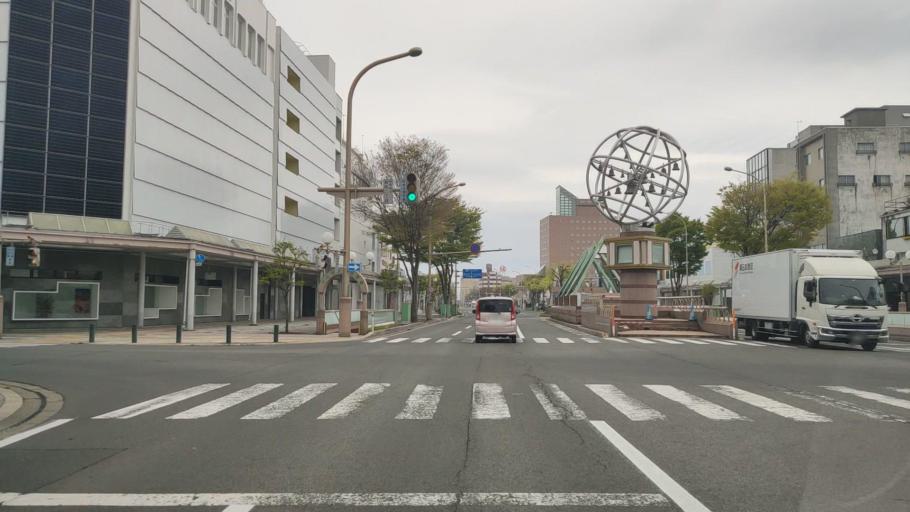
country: JP
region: Aomori
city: Aomori Shi
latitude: 40.8243
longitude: 140.7453
